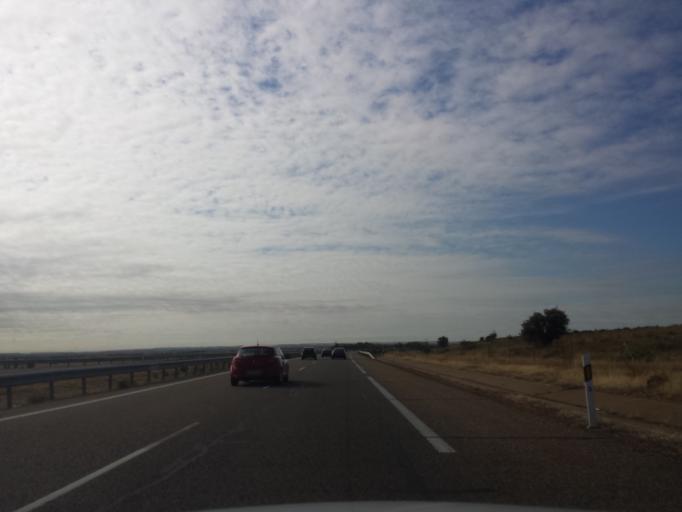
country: ES
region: Castille and Leon
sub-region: Provincia de Leon
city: Ardon
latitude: 42.4714
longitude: -5.5885
